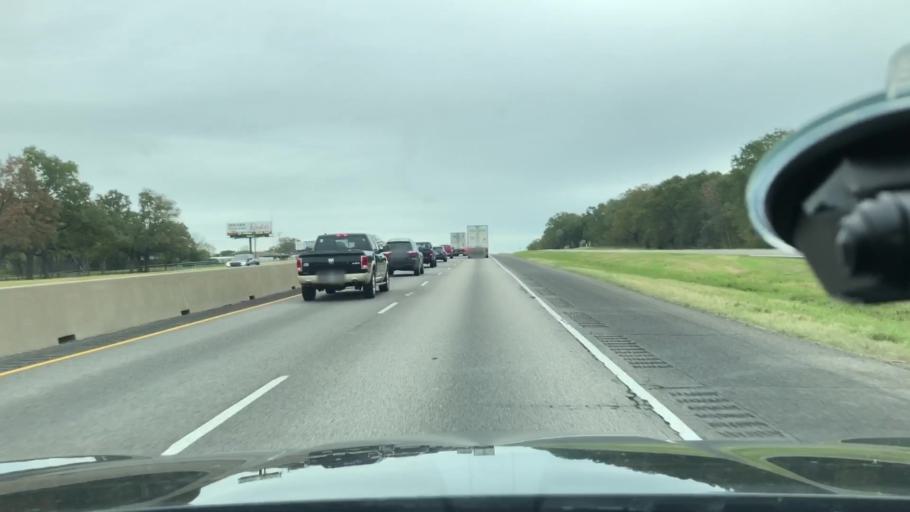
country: US
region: Texas
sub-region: Hopkins County
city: Sulphur Springs
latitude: 33.1470
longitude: -95.5432
